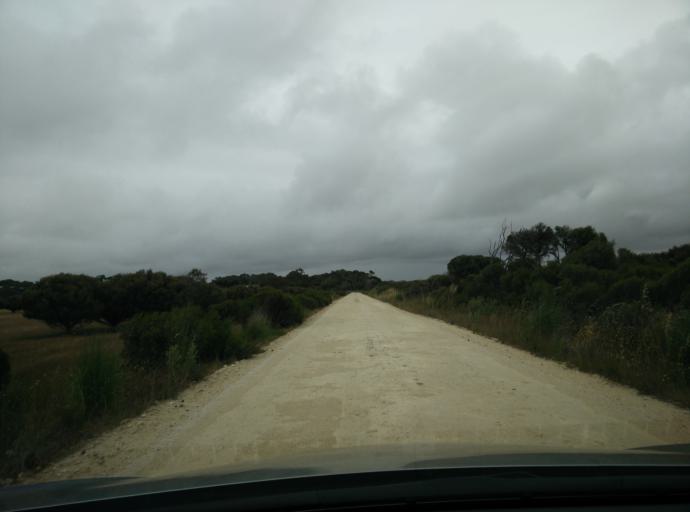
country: AU
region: South Australia
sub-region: Kangaroo Island
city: Kingscote
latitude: -35.8488
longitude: 137.5530
